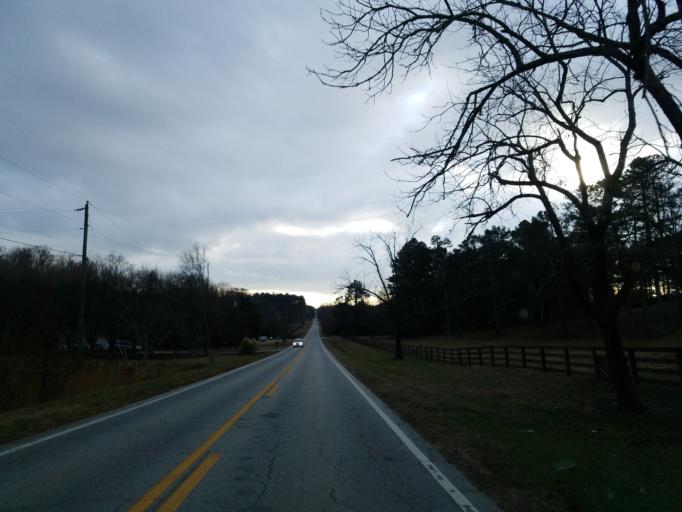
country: US
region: Georgia
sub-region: Dawson County
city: Dawsonville
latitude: 34.3438
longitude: -84.0607
